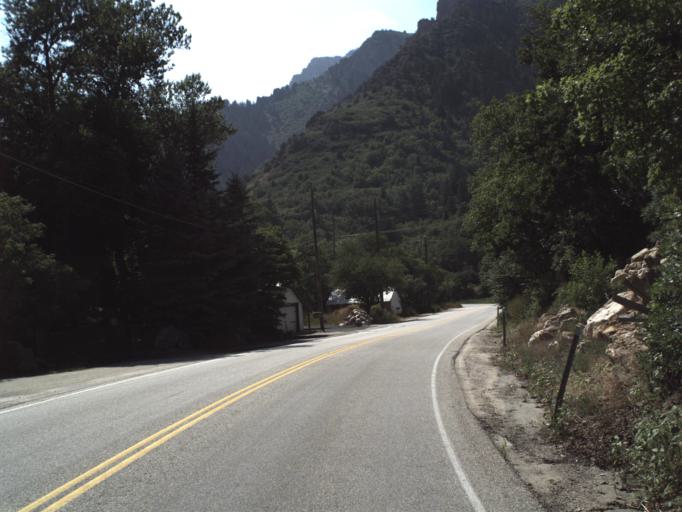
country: US
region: Utah
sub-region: Weber County
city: Liberty
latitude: 41.2551
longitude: -111.8636
